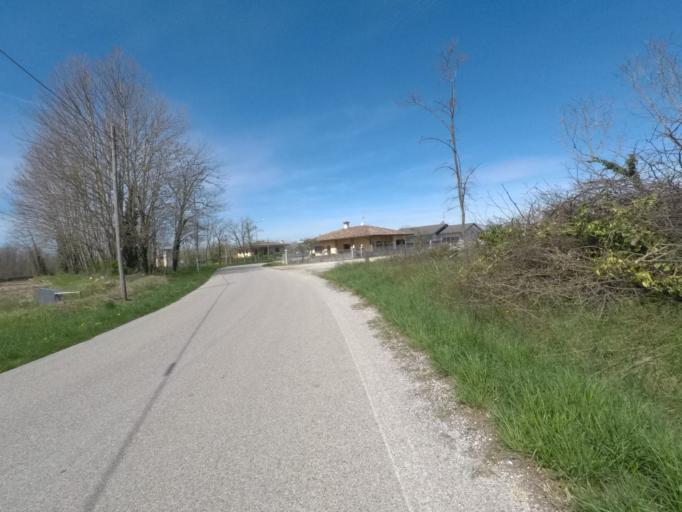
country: IT
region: Friuli Venezia Giulia
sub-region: Provincia di Udine
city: Camino al Tagliamento
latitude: 45.9501
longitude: 12.9388
